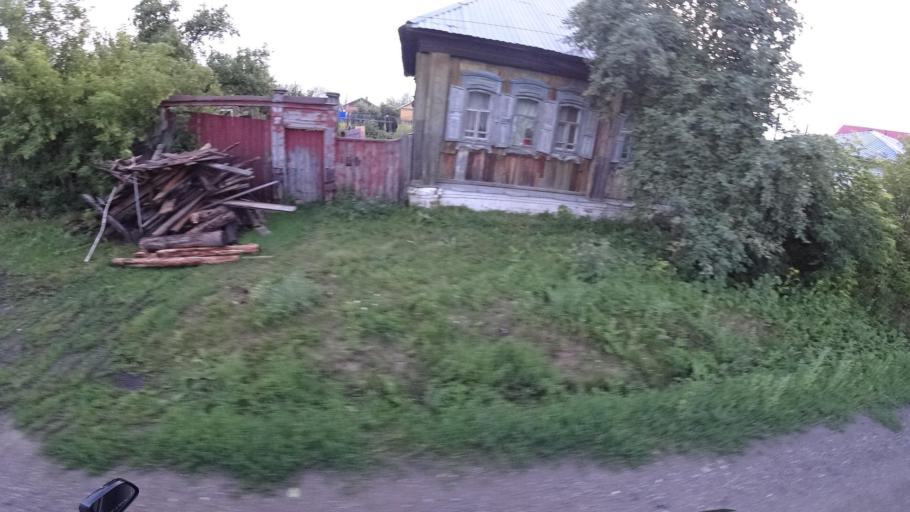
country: RU
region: Sverdlovsk
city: Kamyshlov
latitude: 56.8611
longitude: 62.7133
